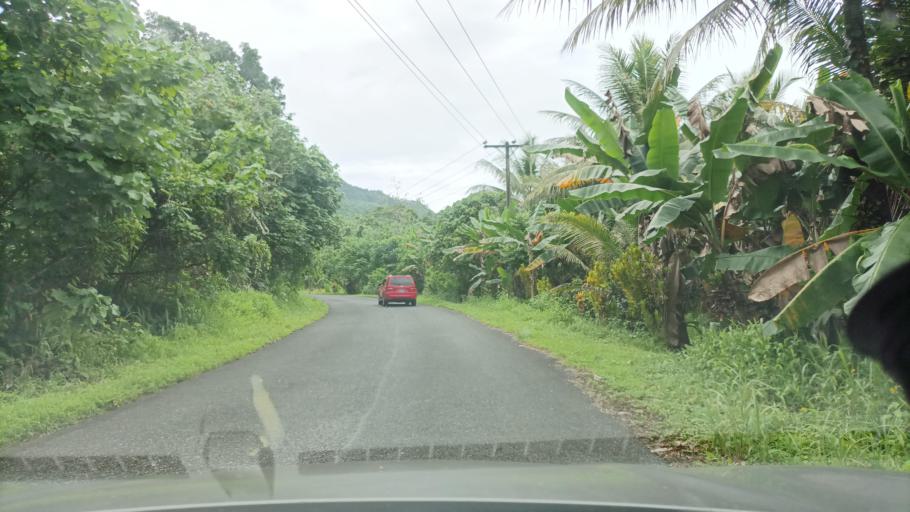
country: FM
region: Pohnpei
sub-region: Madolenihm Municipality
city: Madolenihm Municipality Government
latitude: 6.8908
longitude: 158.3035
